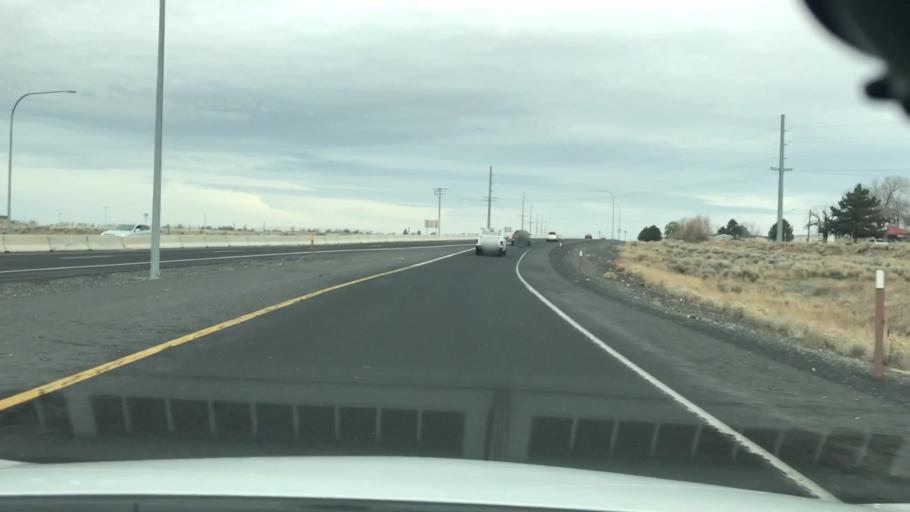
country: US
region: Washington
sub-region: Grant County
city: Moses Lake
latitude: 47.1439
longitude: -119.2824
